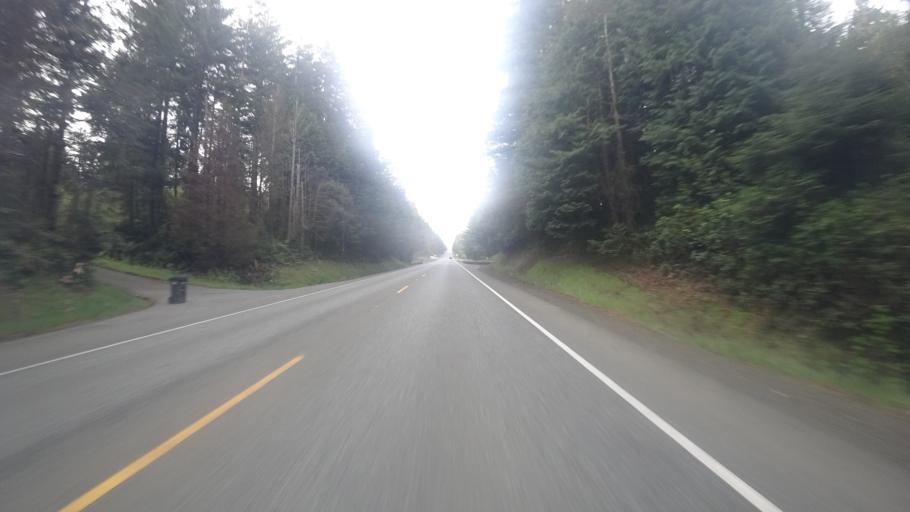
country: US
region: Oregon
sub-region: Coos County
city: Lakeside
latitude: 43.5304
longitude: -124.2158
